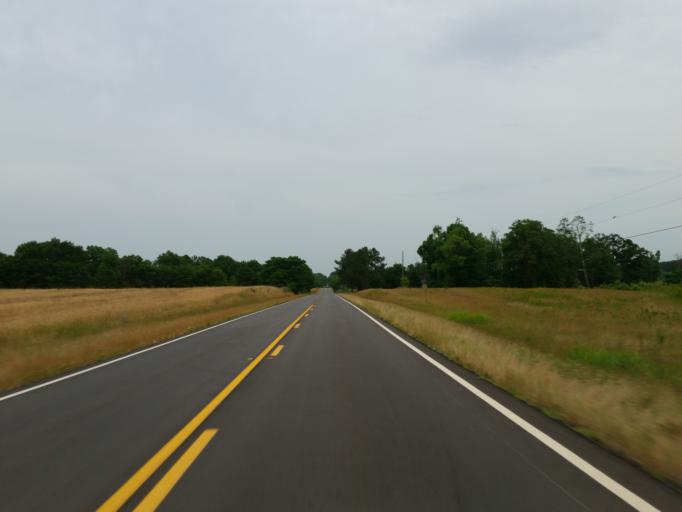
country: US
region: Georgia
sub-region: Dooly County
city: Unadilla
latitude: 32.3100
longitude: -83.7684
